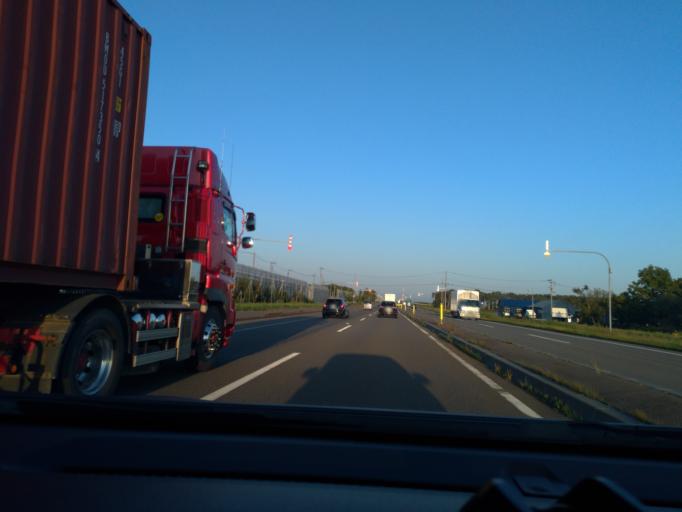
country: JP
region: Hokkaido
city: Tobetsu
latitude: 43.1803
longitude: 141.4753
